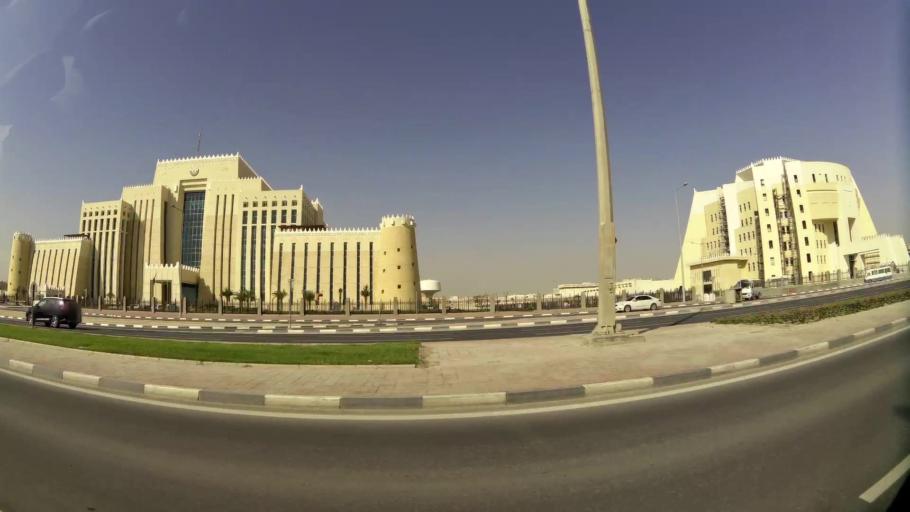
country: QA
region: Baladiyat ad Dawhah
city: Doha
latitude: 25.3069
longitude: 51.5055
